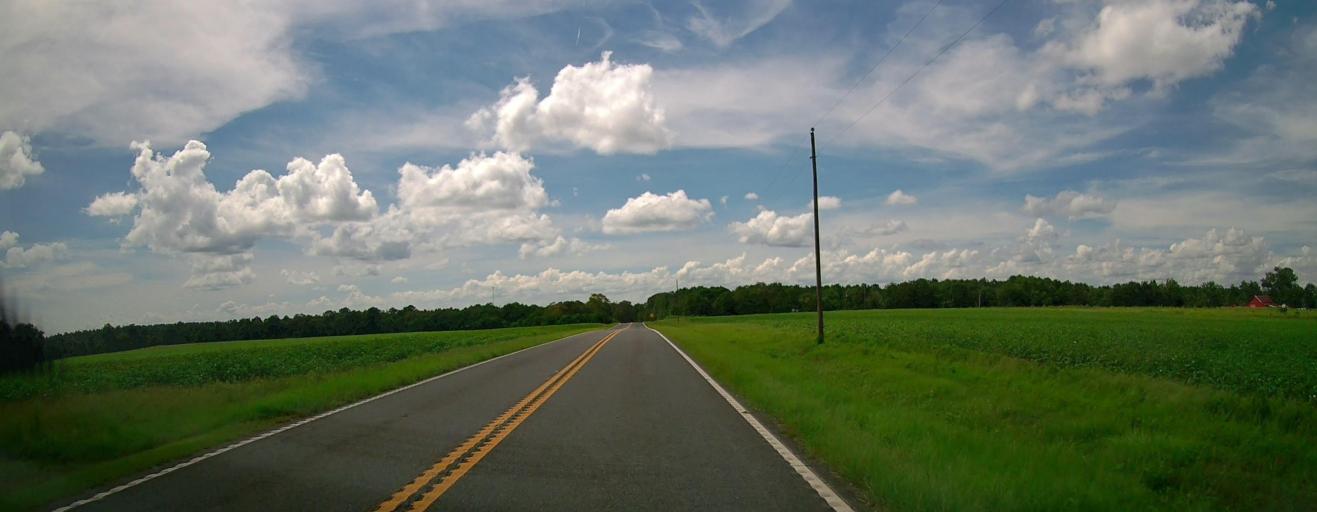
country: US
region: Georgia
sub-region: Taylor County
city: Reynolds
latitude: 32.4403
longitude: -84.1395
